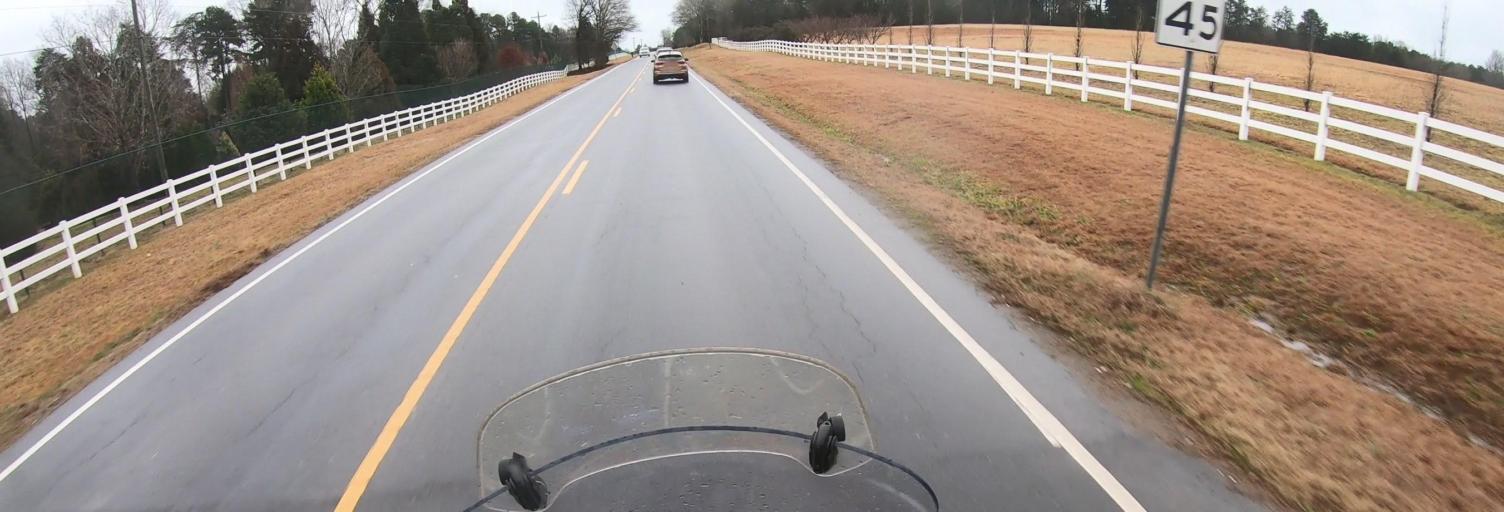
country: US
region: South Carolina
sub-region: York County
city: Lake Wylie
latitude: 35.0784
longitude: -81.0057
